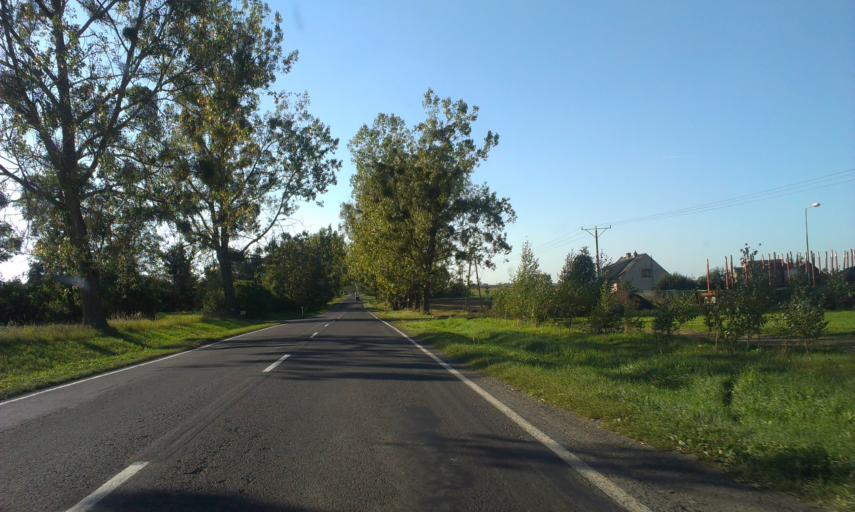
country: PL
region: Kujawsko-Pomorskie
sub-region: Powiat swiecki
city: Drzycim
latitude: 53.4231
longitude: 18.3351
